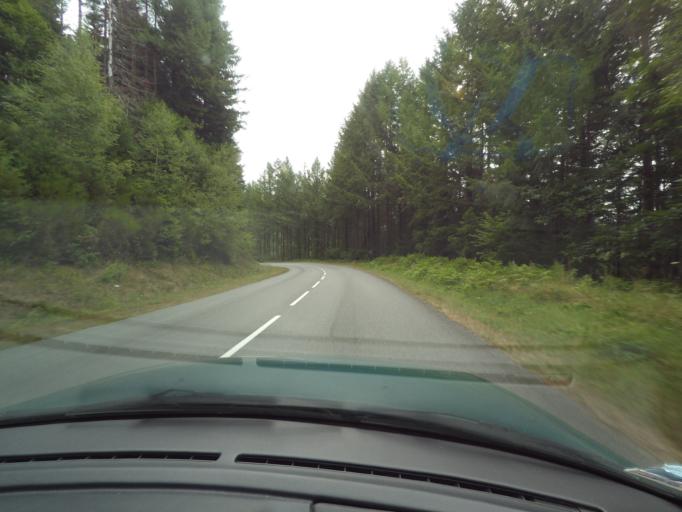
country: FR
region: Limousin
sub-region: Departement de la Haute-Vienne
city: Eymoutiers
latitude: 45.7239
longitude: 1.7984
